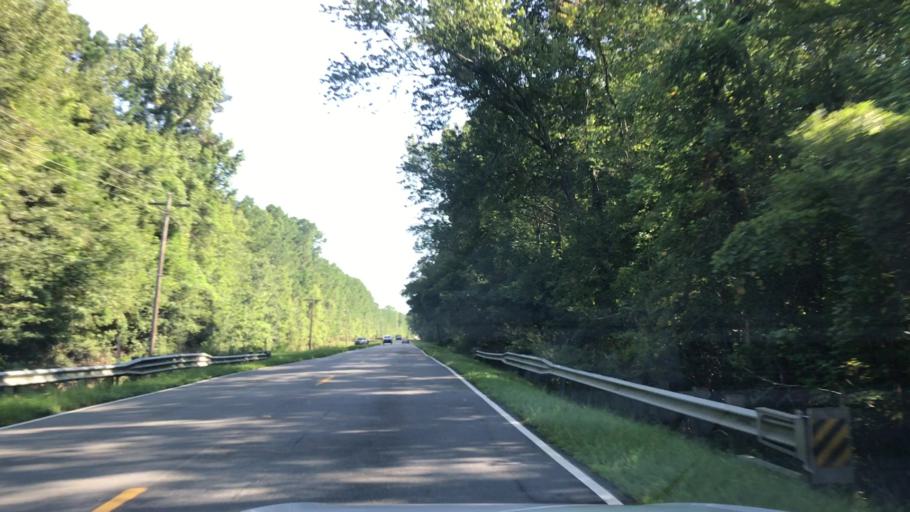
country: US
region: South Carolina
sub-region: Georgetown County
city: Georgetown
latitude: 33.4908
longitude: -79.2646
